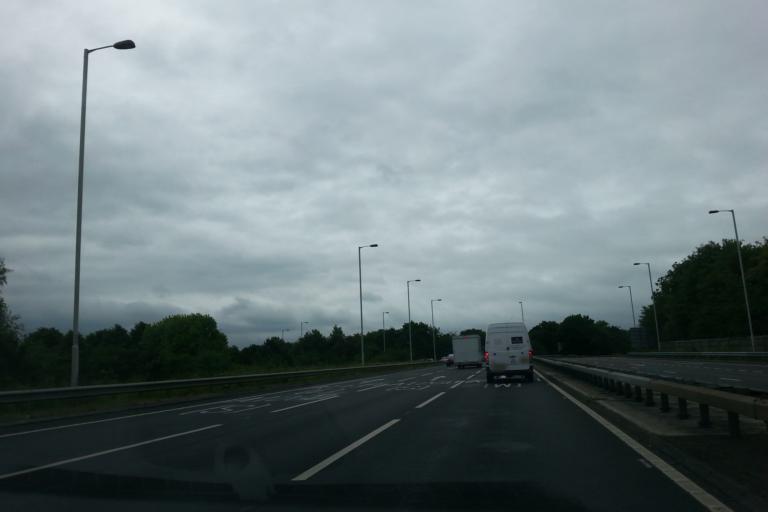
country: GB
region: England
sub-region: Cambridgeshire
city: Yaxley
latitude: 52.5477
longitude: -0.2653
